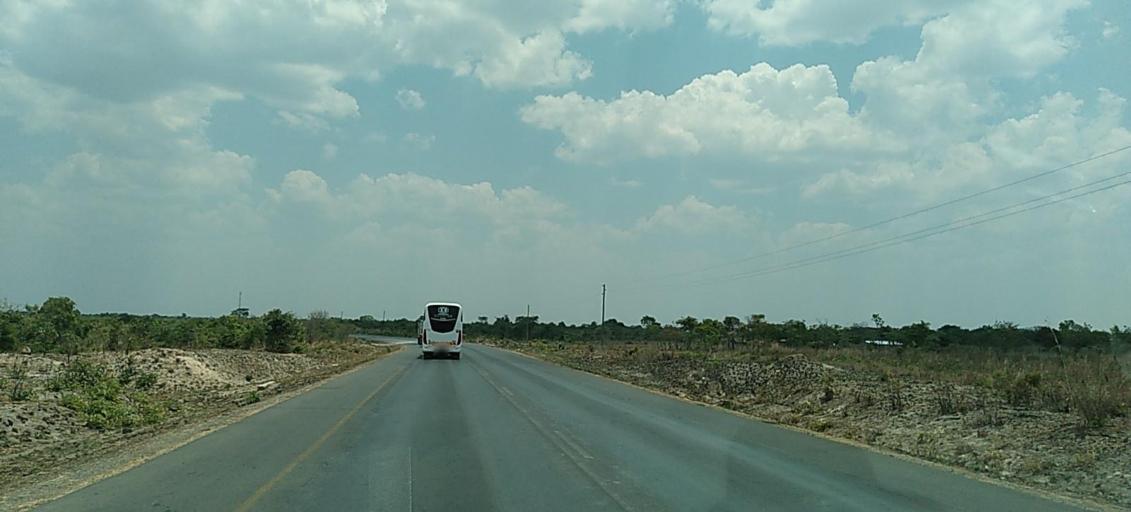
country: ZM
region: Central
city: Kapiri Mposhi
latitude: -14.0547
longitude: 28.6485
